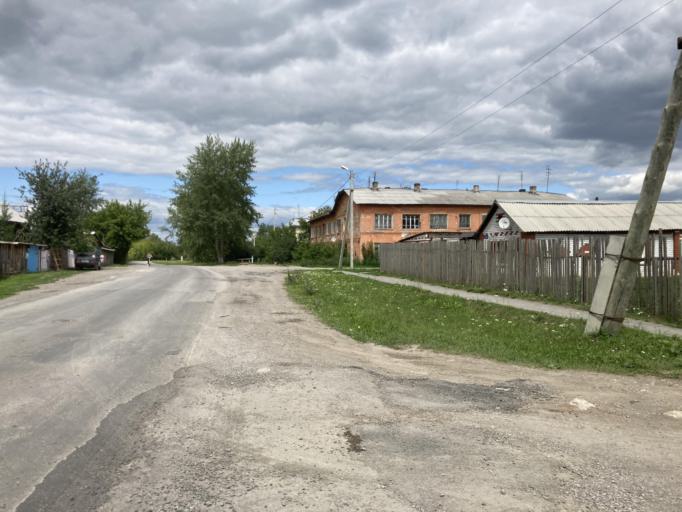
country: RU
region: Sverdlovsk
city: Bogdanovich
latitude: 56.7845
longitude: 62.0665
